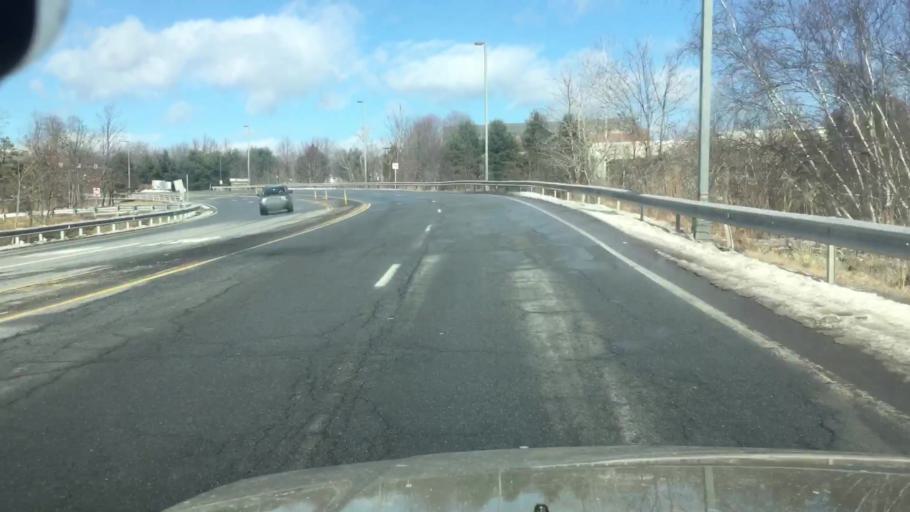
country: US
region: Pennsylvania
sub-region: Luzerne County
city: Hudson
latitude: 41.2491
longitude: -75.8088
